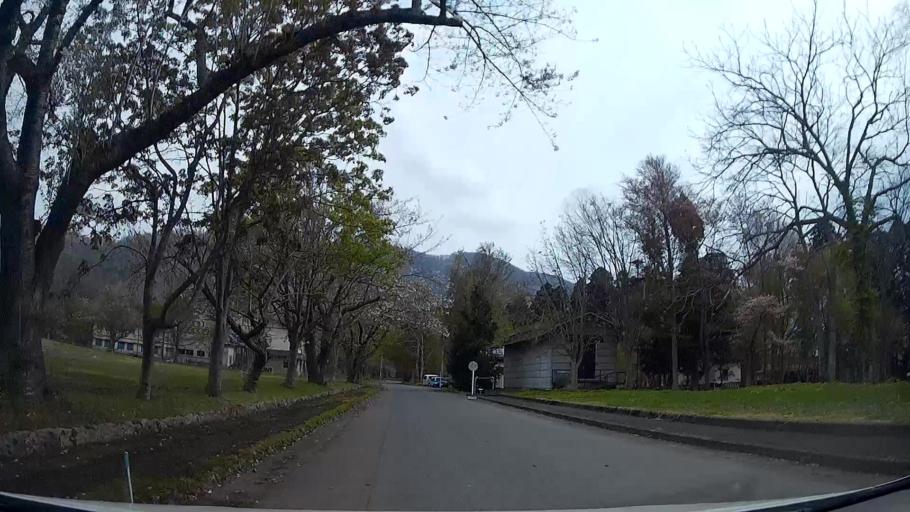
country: JP
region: Akita
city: Hanawa
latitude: 40.4283
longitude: 140.8951
